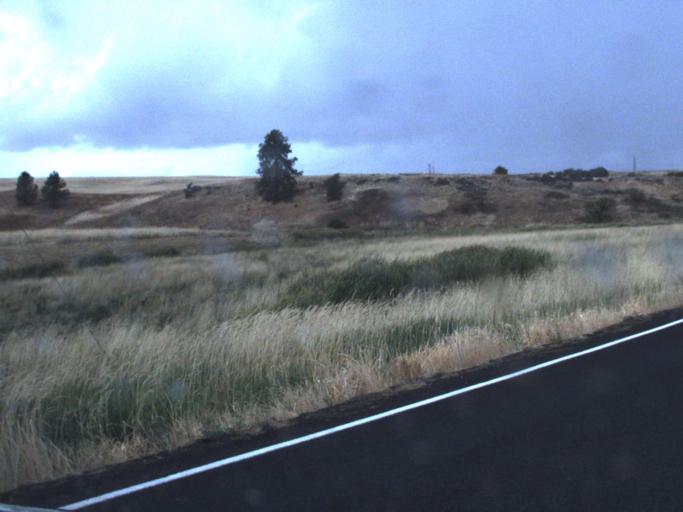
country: US
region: Washington
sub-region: Spokane County
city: Medical Lake
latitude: 47.7192
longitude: -117.8712
